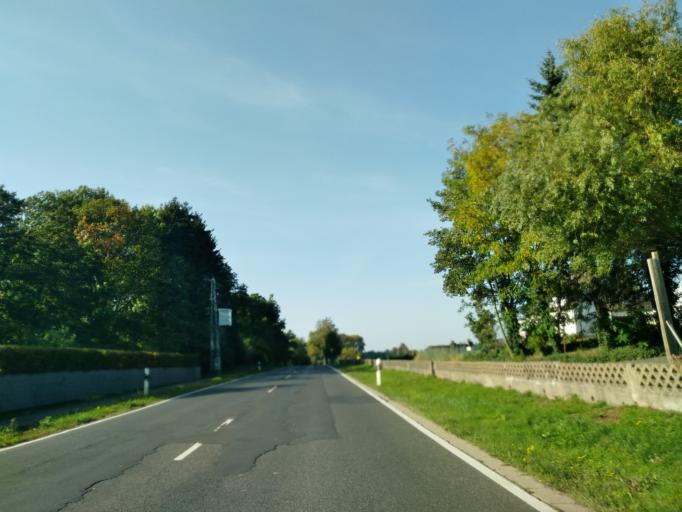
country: DE
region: North Rhine-Westphalia
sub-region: Regierungsbezirk Koln
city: Stossdorf
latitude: 50.7405
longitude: 7.2482
